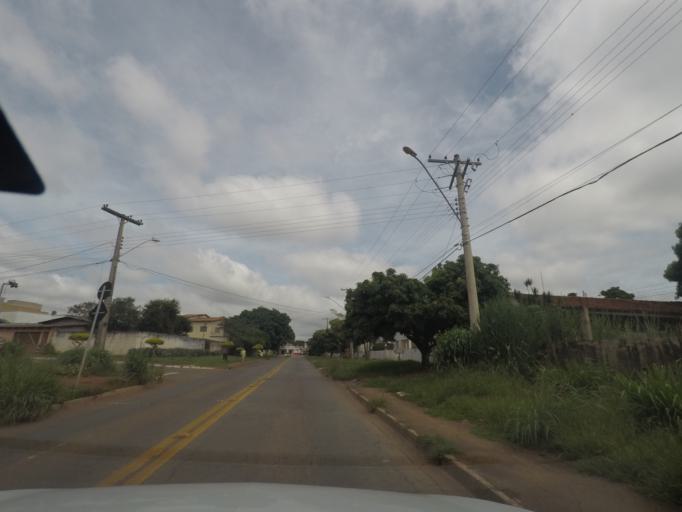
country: BR
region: Goias
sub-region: Goiania
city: Goiania
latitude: -16.6374
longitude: -49.2264
